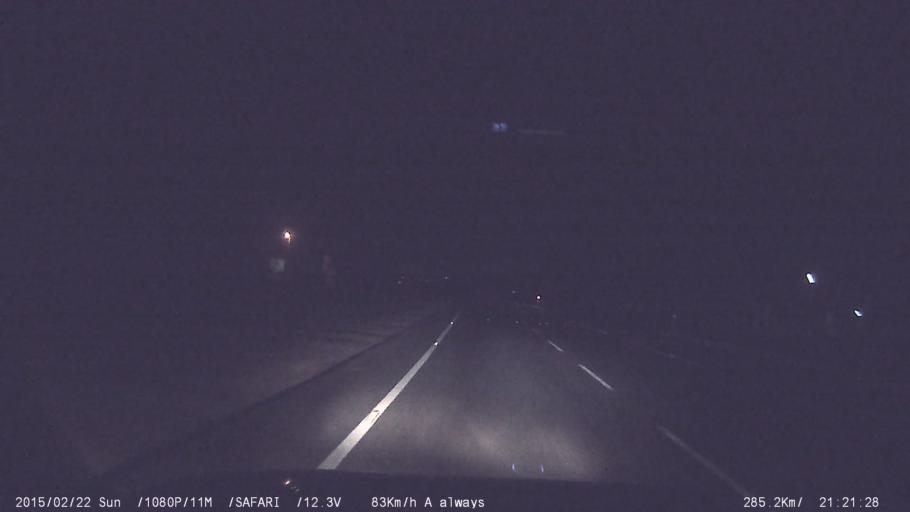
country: IN
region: Tamil Nadu
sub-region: Karur
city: Karur
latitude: 10.8640
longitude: 77.9916
